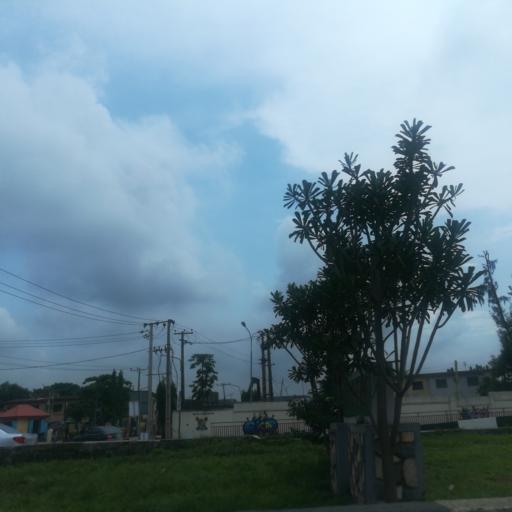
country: NG
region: Lagos
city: Ojota
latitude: 6.5842
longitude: 3.3905
